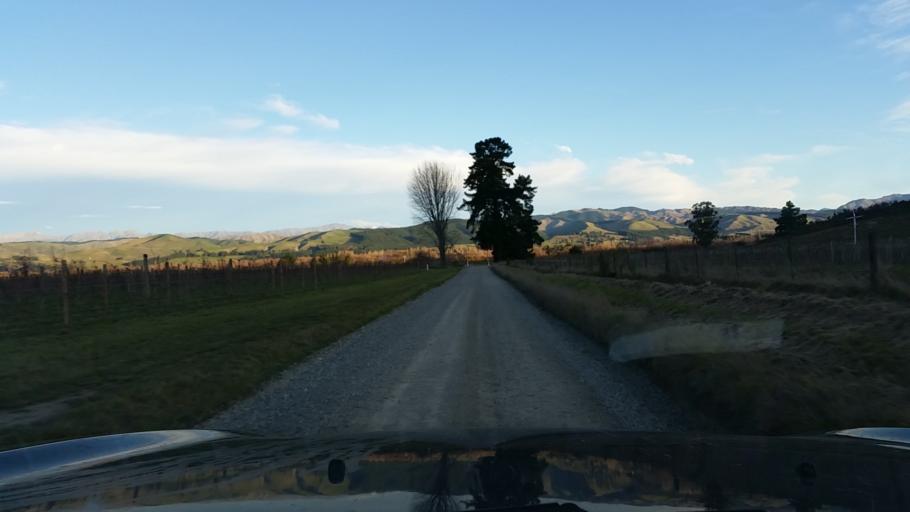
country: NZ
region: Marlborough
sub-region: Marlborough District
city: Blenheim
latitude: -41.5144
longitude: 173.5849
